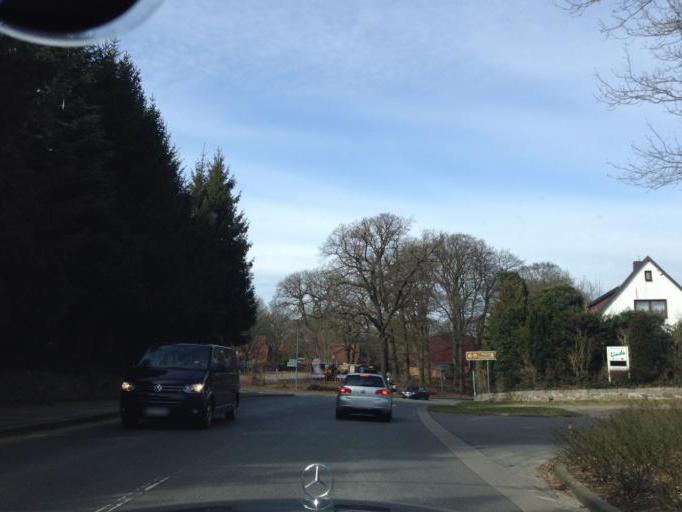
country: DE
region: Lower Saxony
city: Seevetal
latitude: 53.4429
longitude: 9.9036
